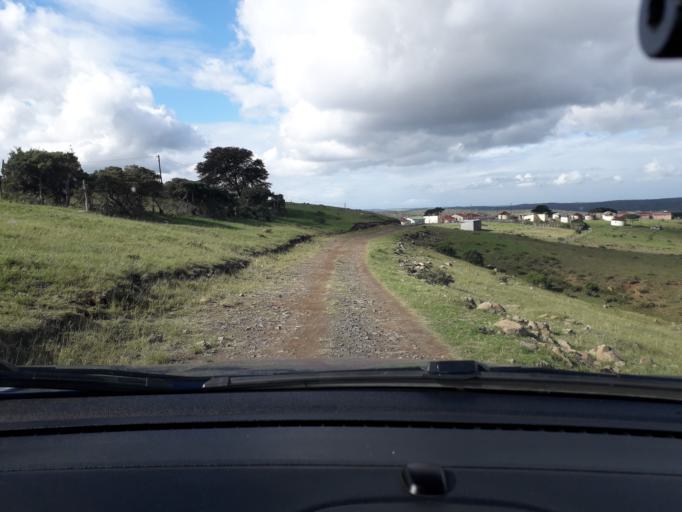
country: ZA
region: Eastern Cape
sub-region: Buffalo City Metropolitan Municipality
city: Bhisho
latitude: -33.1140
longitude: 27.4270
